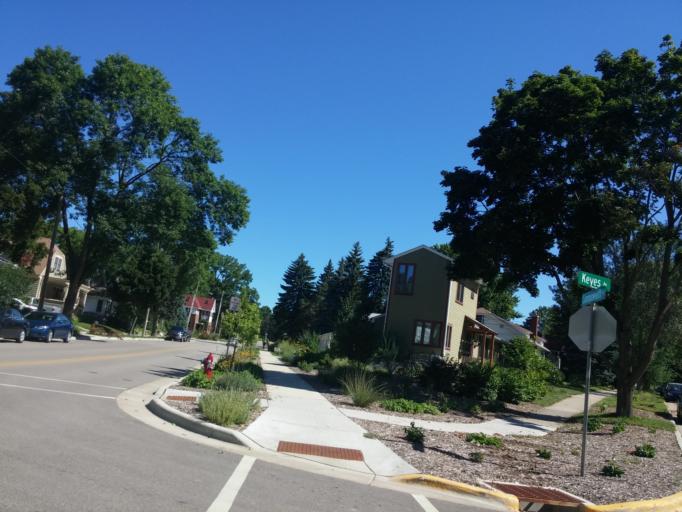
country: US
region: Wisconsin
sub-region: Dane County
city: Shorewood Hills
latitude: 43.0610
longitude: -89.4265
